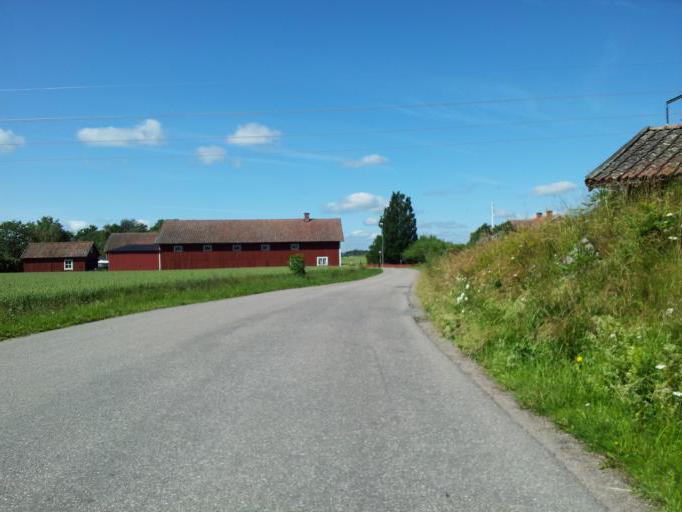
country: SE
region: Uppsala
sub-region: Uppsala Kommun
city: Saevja
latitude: 59.8735
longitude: 17.7278
